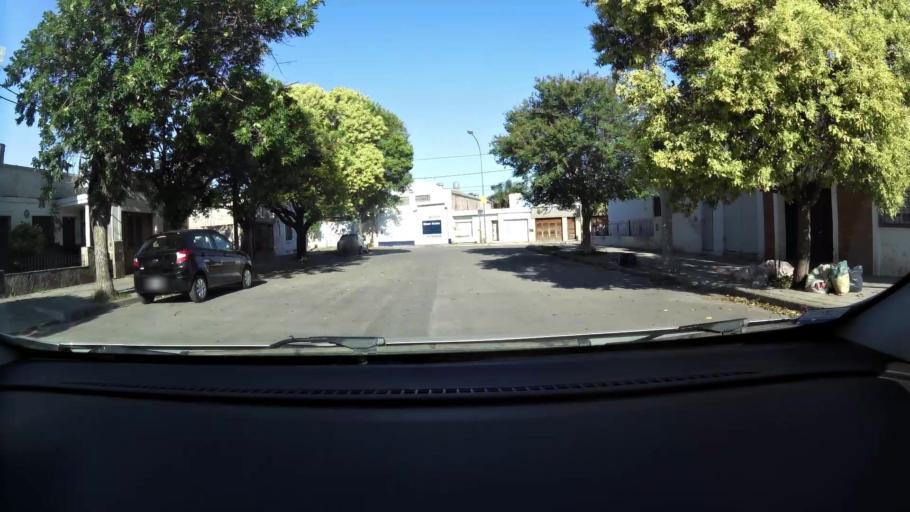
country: AR
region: Cordoba
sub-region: Departamento de Capital
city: Cordoba
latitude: -31.3864
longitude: -64.1769
